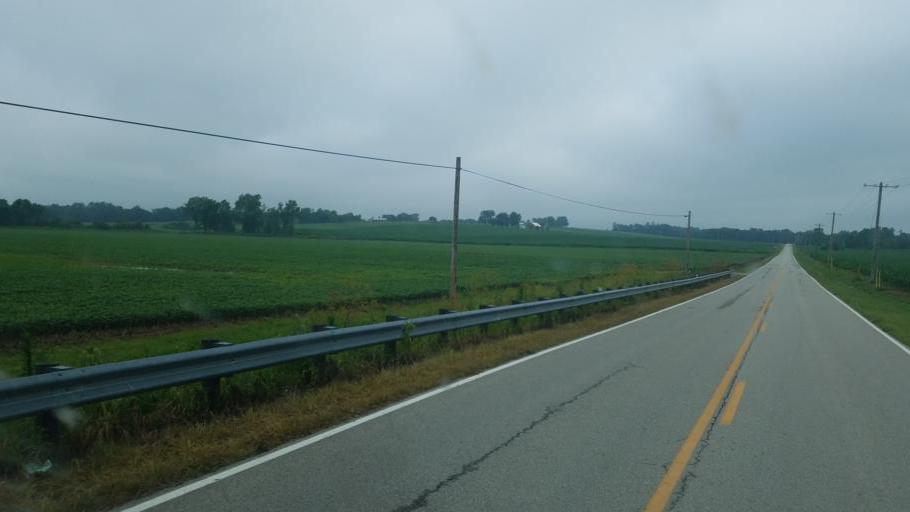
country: US
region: Ohio
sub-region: Highland County
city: Hillsboro
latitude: 39.2303
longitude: -83.5789
